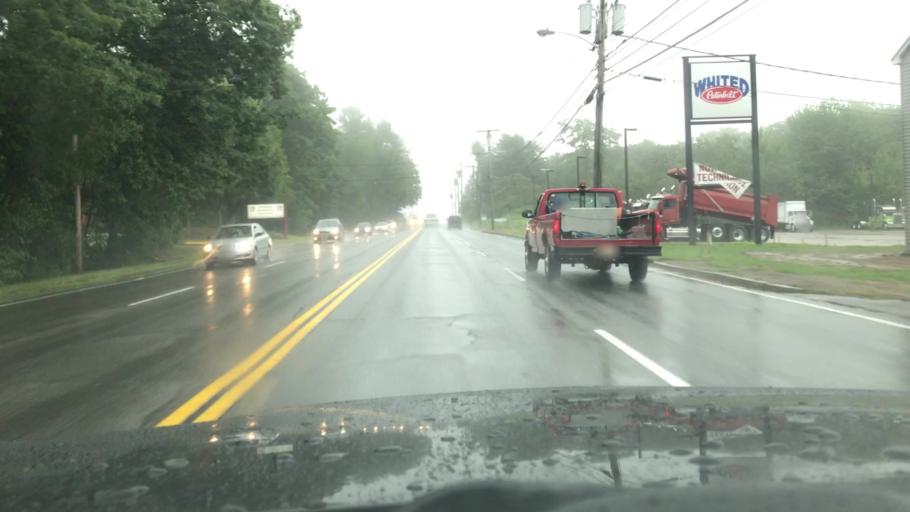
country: US
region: Maine
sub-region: York County
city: Saco
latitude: 43.5355
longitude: -70.4230
